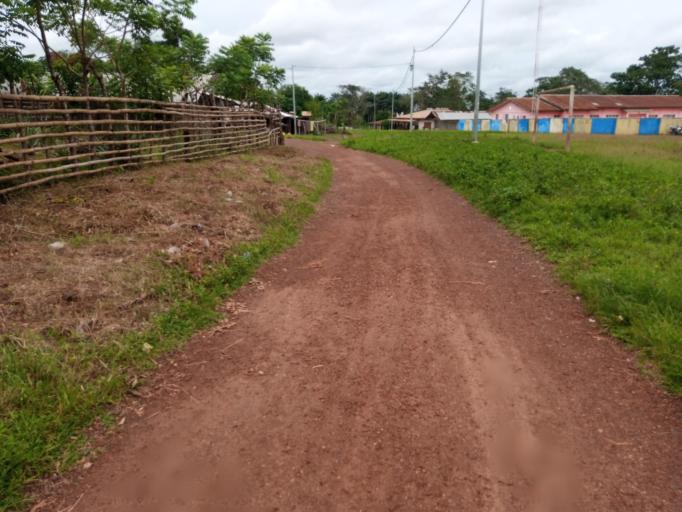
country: SL
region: Southern Province
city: Largo
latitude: 8.2011
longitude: -12.0609
